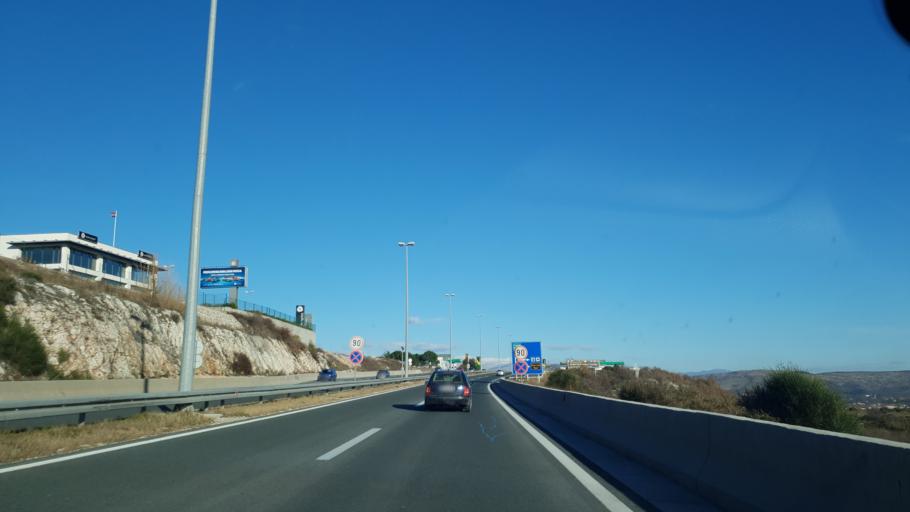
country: HR
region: Splitsko-Dalmatinska
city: Klis
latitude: 43.5818
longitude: 16.5563
